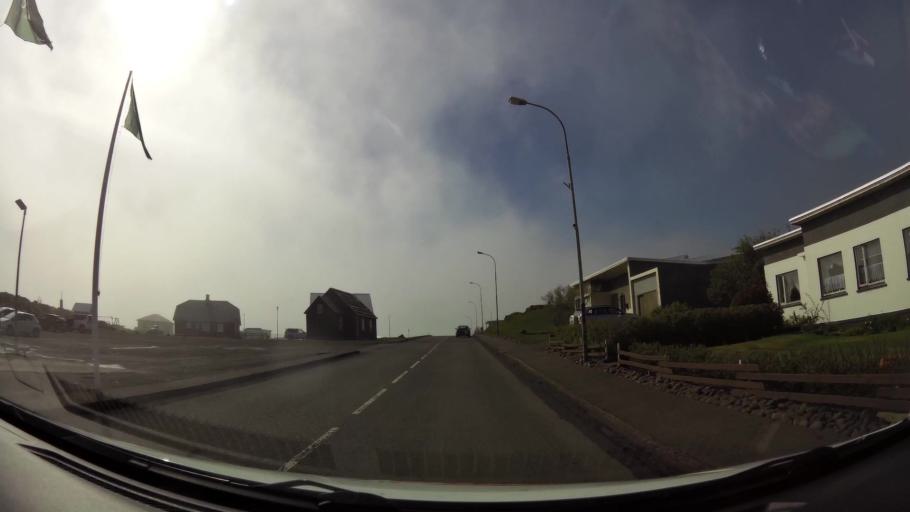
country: IS
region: East
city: Reydarfjoerdur
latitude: 64.6562
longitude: -14.2863
